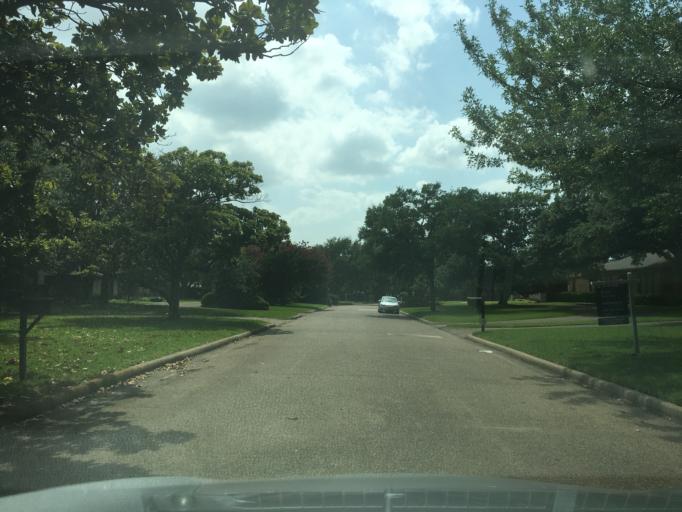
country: US
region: Texas
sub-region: Dallas County
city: University Park
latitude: 32.8981
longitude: -96.8162
